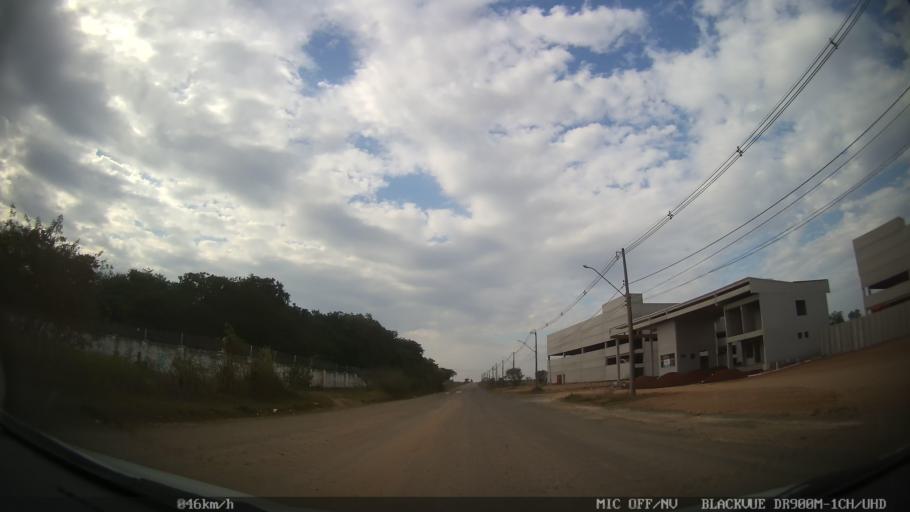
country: BR
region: Sao Paulo
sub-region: Paulinia
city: Paulinia
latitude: -22.7223
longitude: -47.1617
